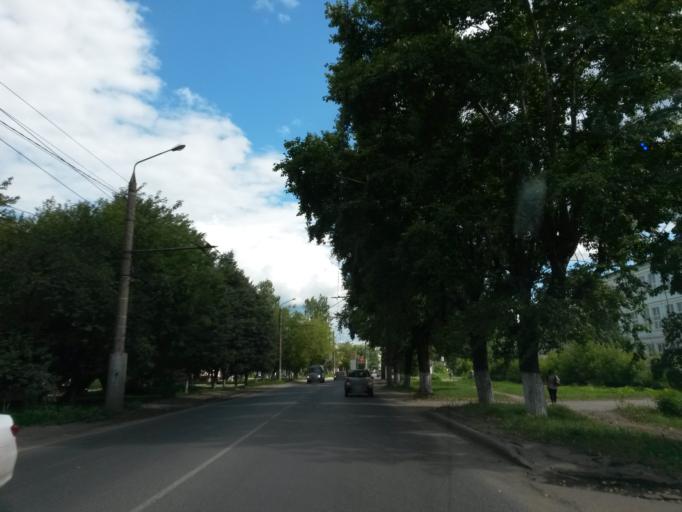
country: RU
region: Ivanovo
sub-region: Gorod Ivanovo
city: Ivanovo
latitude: 56.9978
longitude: 40.9549
